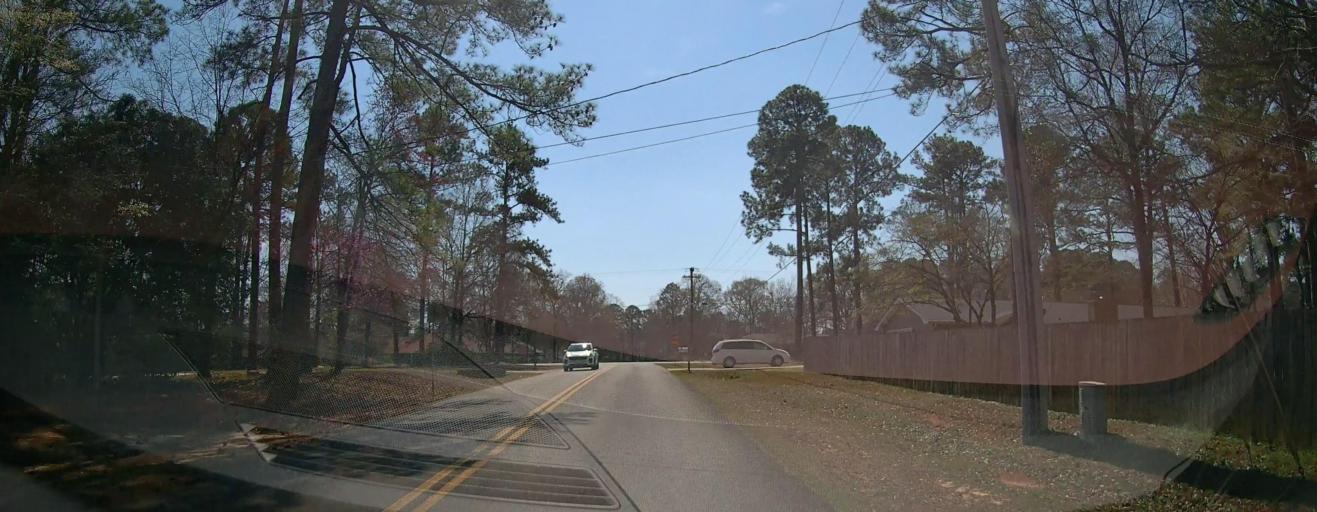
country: US
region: Georgia
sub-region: Houston County
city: Centerville
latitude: 32.5940
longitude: -83.6960
